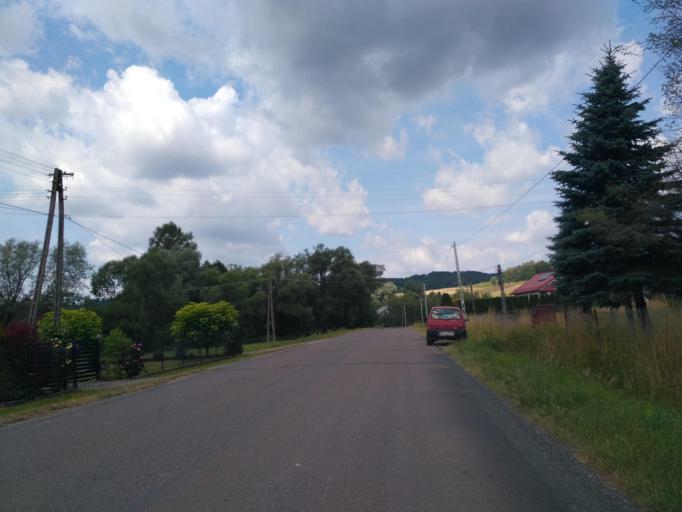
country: PL
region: Subcarpathian Voivodeship
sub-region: Powiat debicki
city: Brzostek
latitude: 49.9238
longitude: 21.3941
